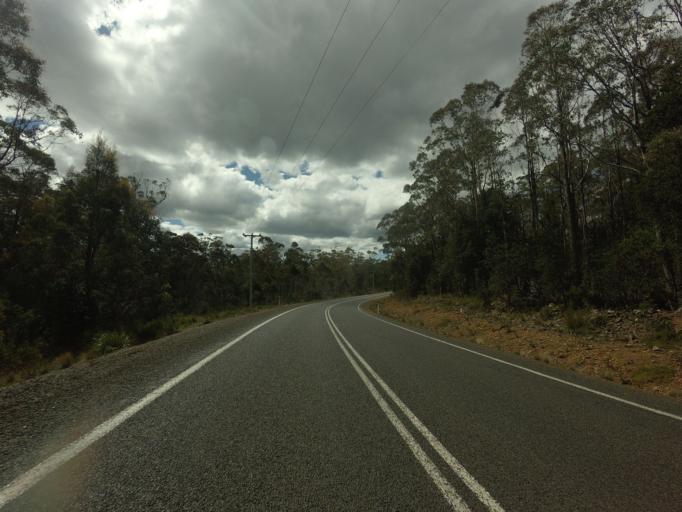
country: AU
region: Tasmania
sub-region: Northern Midlands
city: Evandale
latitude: -42.0053
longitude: 147.7231
